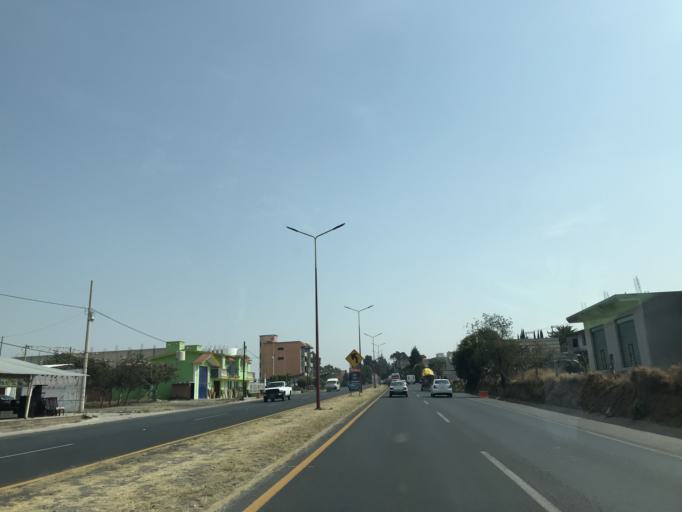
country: MX
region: Tlaxcala
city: La Magdalena Tlaltelulco
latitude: 19.2729
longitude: -98.1973
